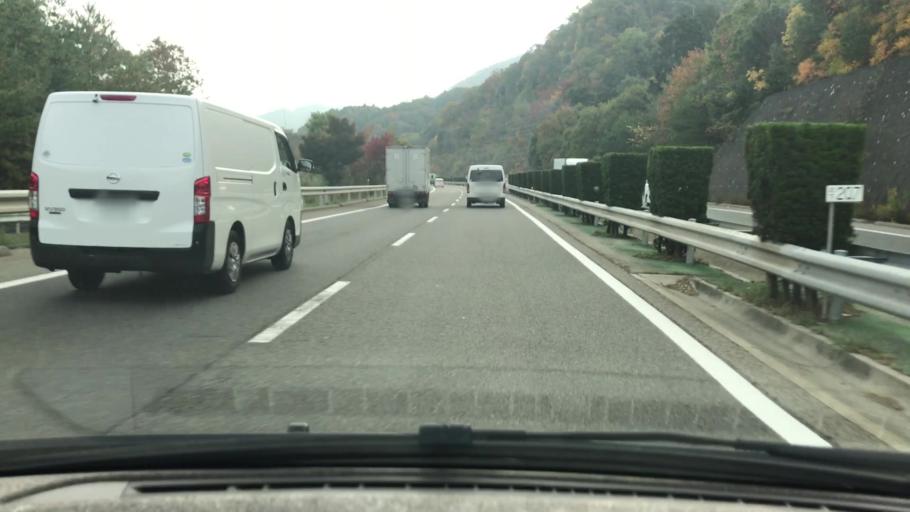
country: JP
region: Hyogo
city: Kobe
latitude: 34.7615
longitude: 135.1812
